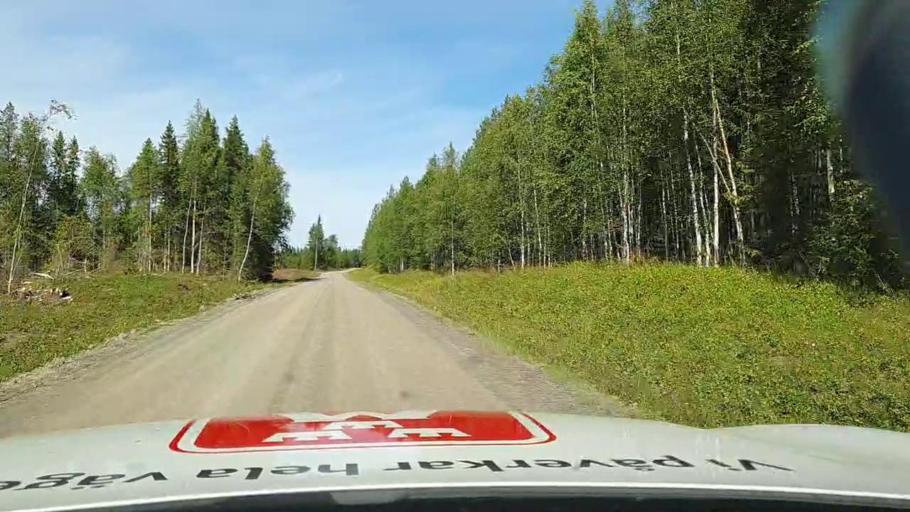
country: SE
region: Jaemtland
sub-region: Stroemsunds Kommun
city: Stroemsund
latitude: 63.7365
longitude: 15.2423
